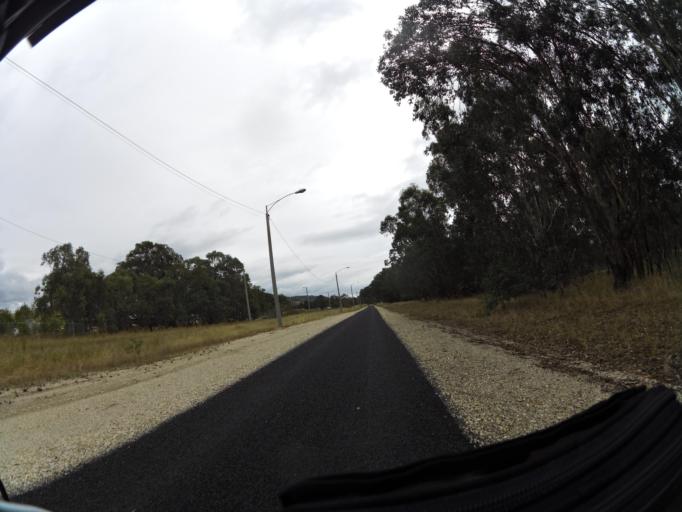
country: AU
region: Victoria
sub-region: Wodonga
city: Wodonga
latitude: -36.1491
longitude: 146.9355
